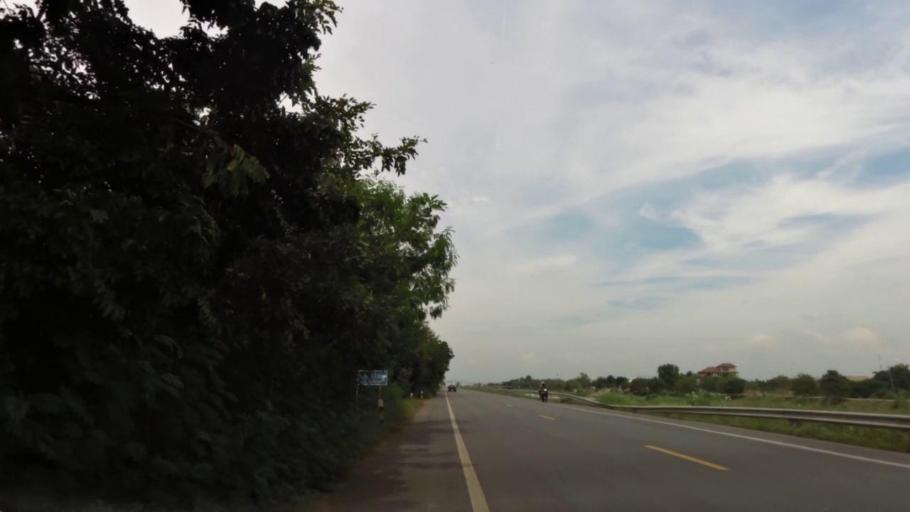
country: TH
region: Lop Buri
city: Ban Mi
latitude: 15.0406
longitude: 100.5654
